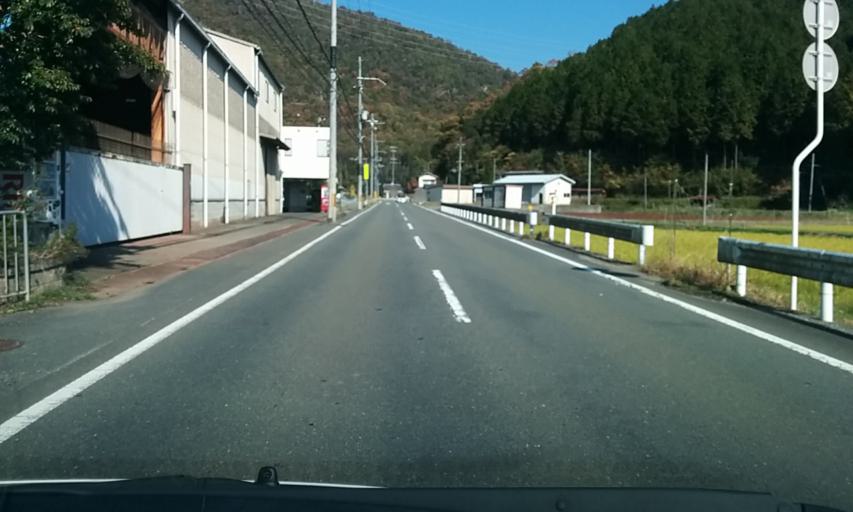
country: JP
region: Kyoto
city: Kameoka
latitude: 35.1323
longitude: 135.4860
